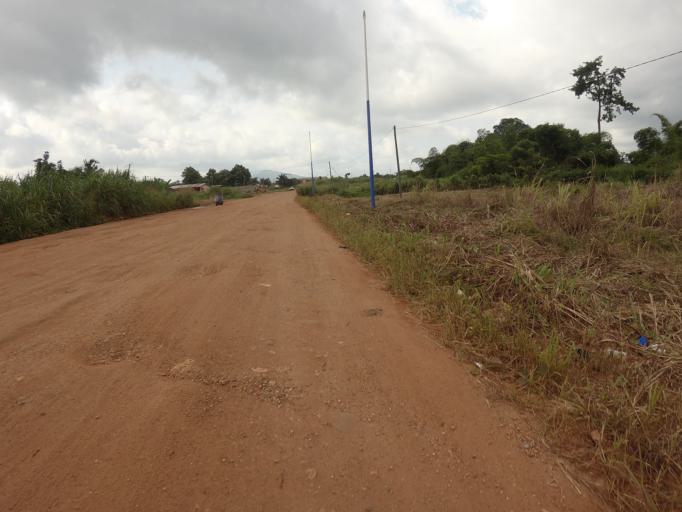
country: GH
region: Volta
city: Hohoe
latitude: 7.1280
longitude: 0.4611
